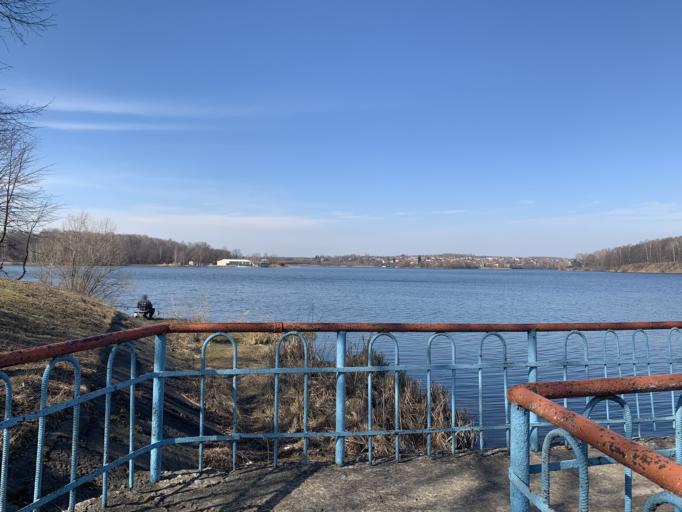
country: RU
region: Kursk
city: Zheleznogorsk
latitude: 52.3180
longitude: 35.3611
